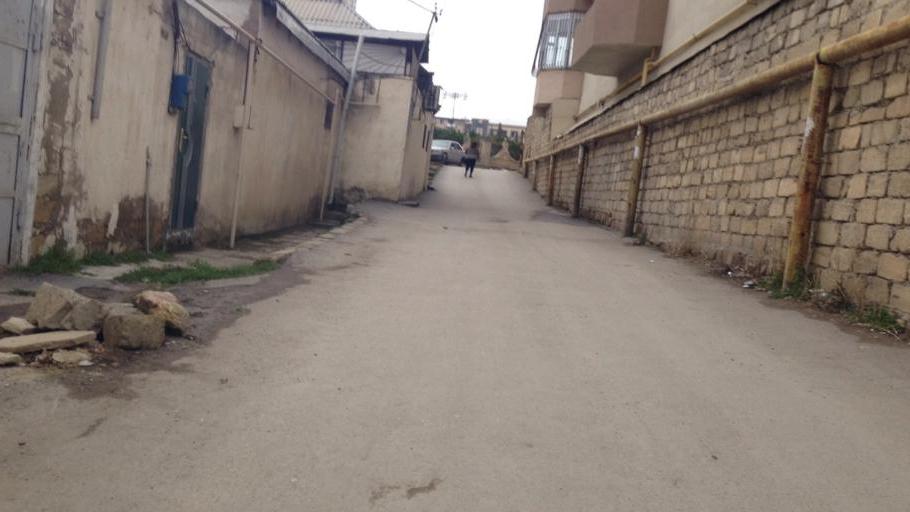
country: AZ
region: Baki
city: Khodzhi-Gasan
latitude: 40.3906
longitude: 49.8099
